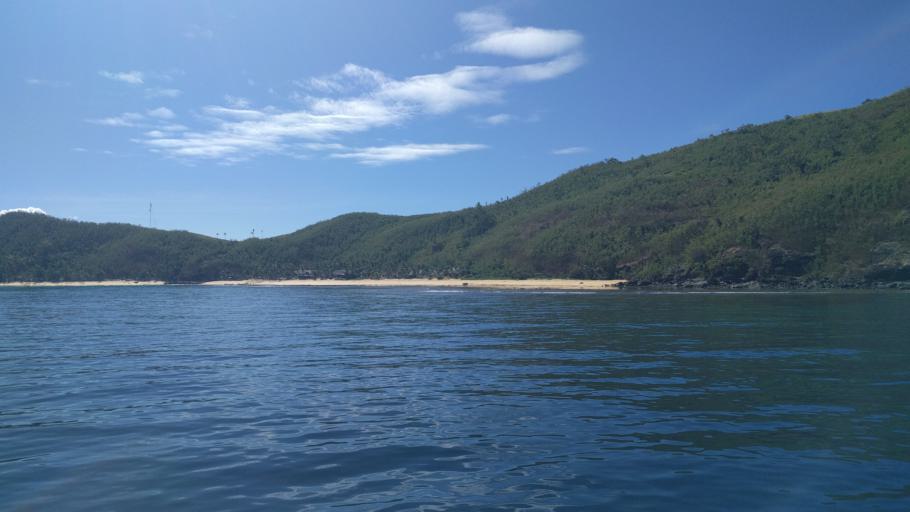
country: FJ
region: Western
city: Lautoka
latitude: -17.2802
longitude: 177.1032
